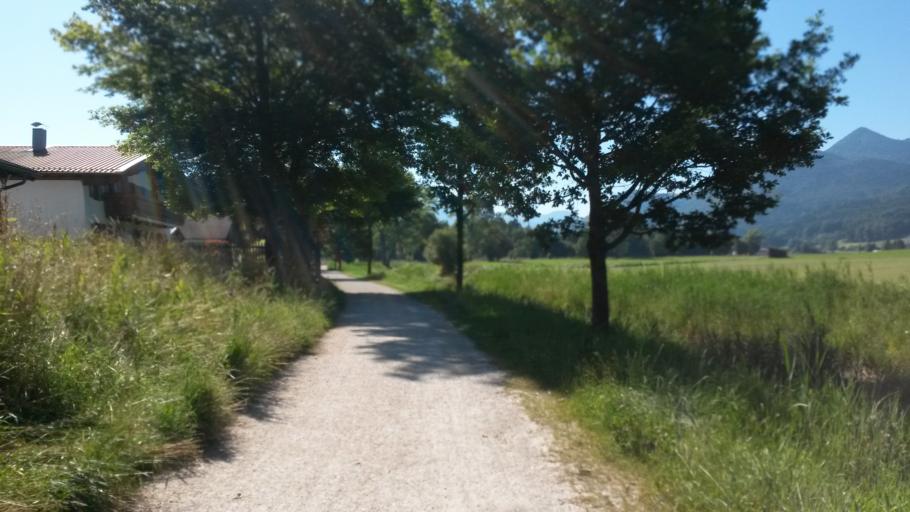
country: DE
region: Bavaria
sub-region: Upper Bavaria
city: Bernau am Chiemsee
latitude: 47.8133
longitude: 12.3863
